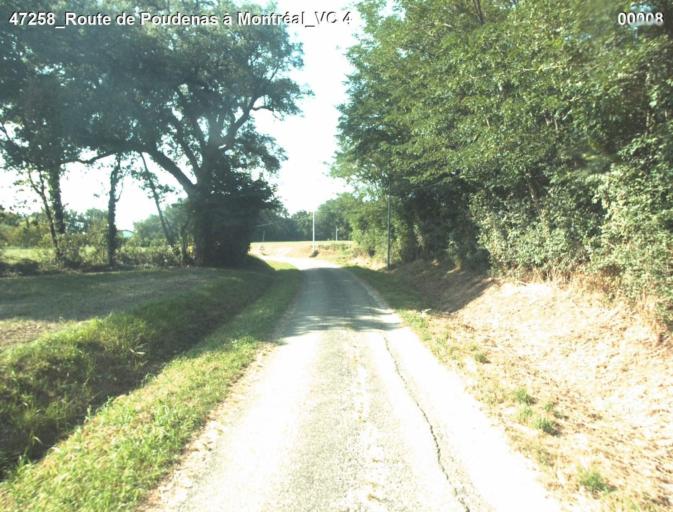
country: FR
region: Midi-Pyrenees
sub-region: Departement du Gers
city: Montreal
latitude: 44.0052
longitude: 0.1826
